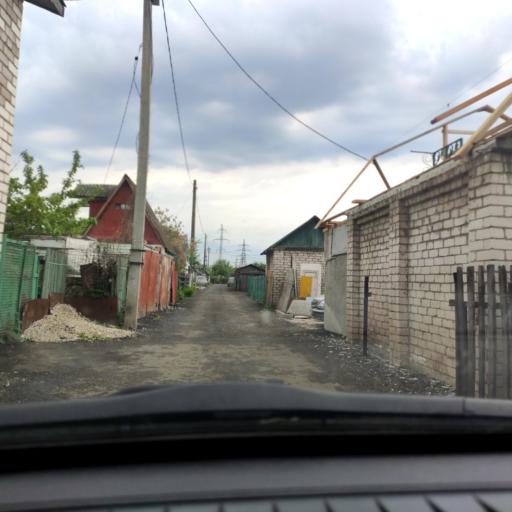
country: RU
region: Samara
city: Tol'yatti
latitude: 53.5430
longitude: 49.4393
